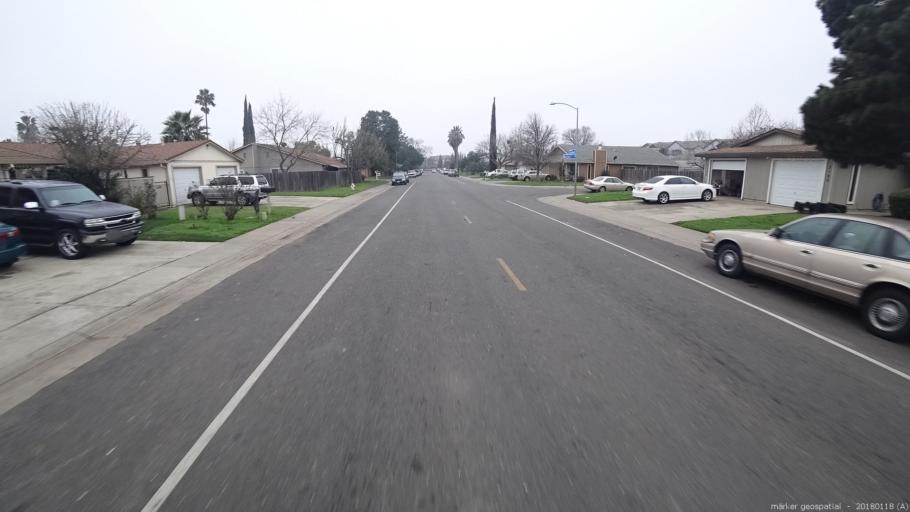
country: US
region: California
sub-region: Sacramento County
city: Rancho Cordova
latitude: 38.5798
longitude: -121.3034
